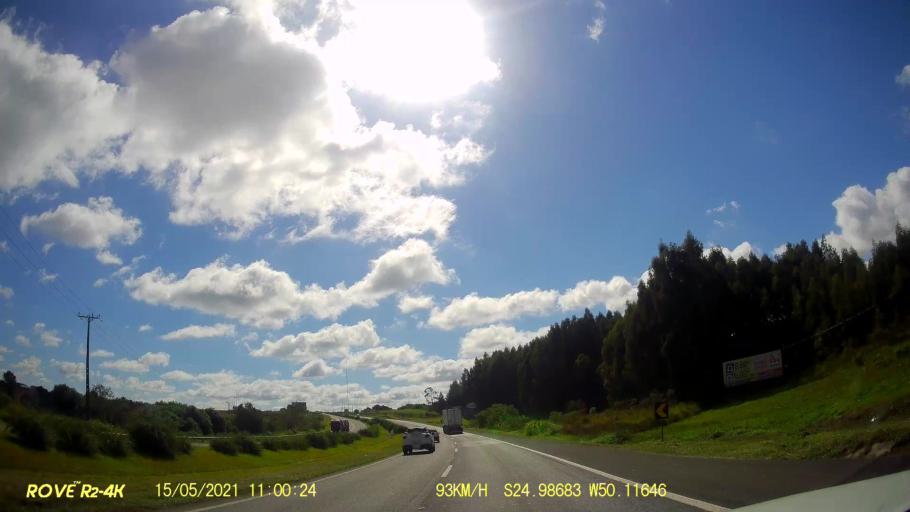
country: BR
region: Parana
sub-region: Carambei
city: Carambei
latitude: -24.9871
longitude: -50.1163
